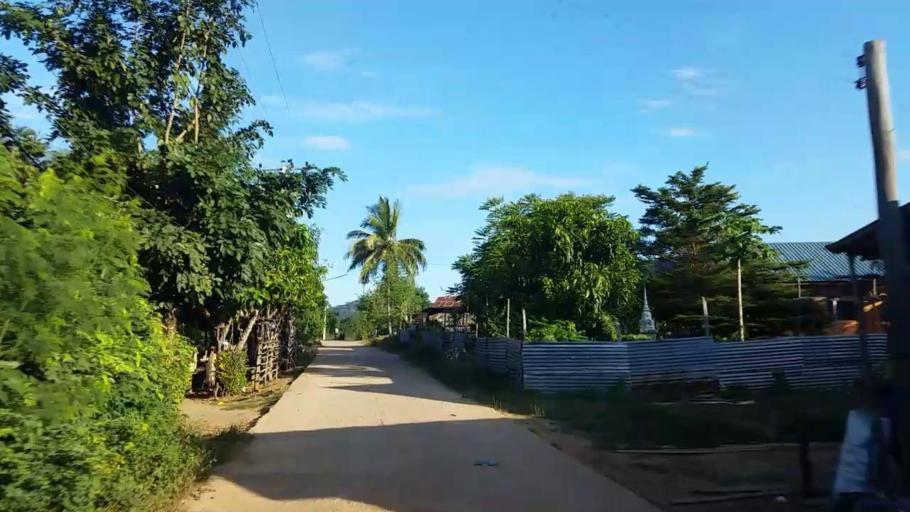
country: TH
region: Chaiyaphum
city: Thep Sathit
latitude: 15.5466
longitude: 101.4789
